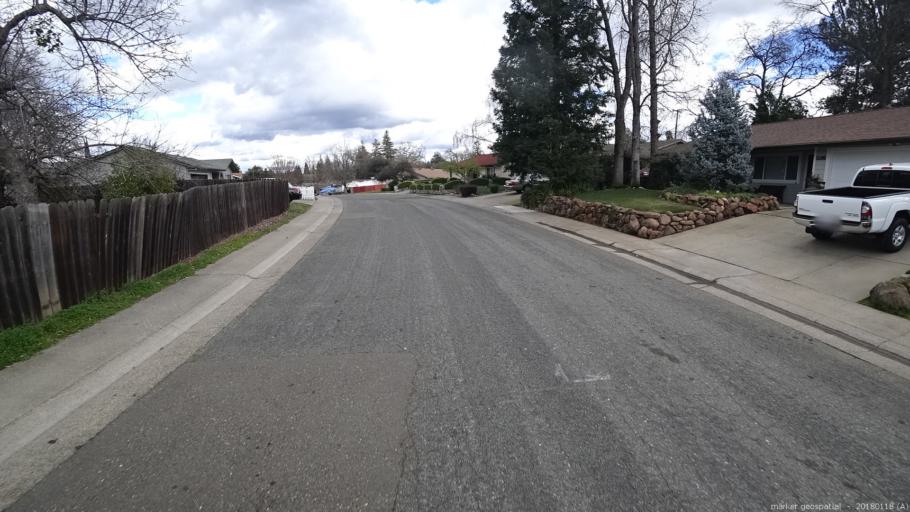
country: US
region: California
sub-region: Sacramento County
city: Orangevale
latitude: 38.6664
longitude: -121.2161
